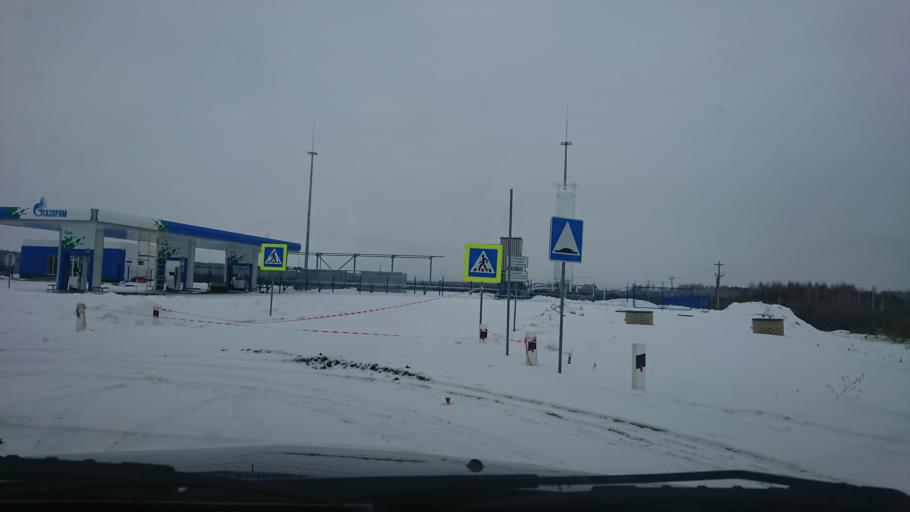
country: RU
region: Chelyabinsk
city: Tyubuk
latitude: 56.0511
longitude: 60.9854
